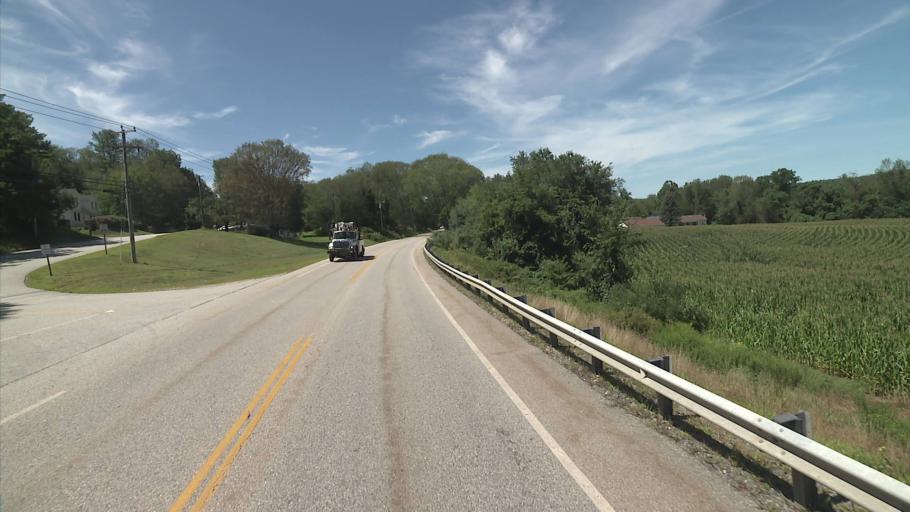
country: US
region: Connecticut
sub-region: Windham County
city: Putnam
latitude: 41.8542
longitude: -71.9527
